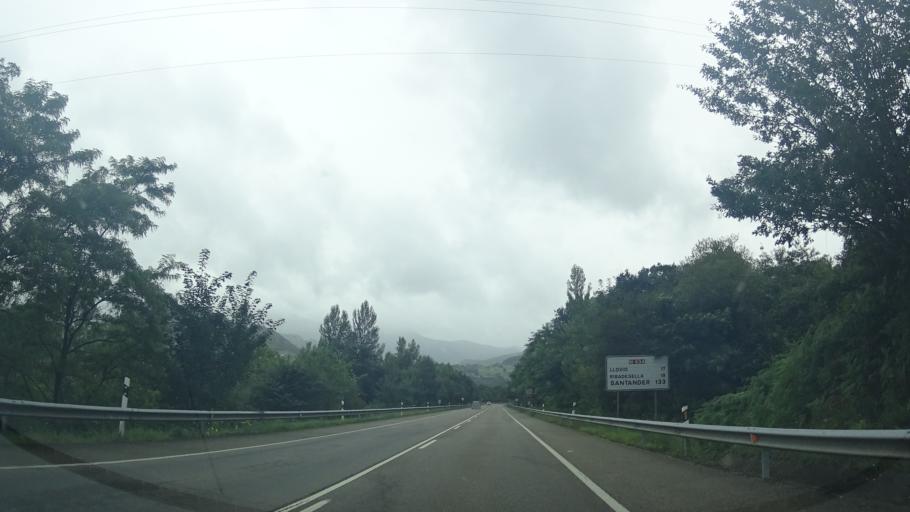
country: ES
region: Asturias
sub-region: Province of Asturias
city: Parres
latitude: 43.3783
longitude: -5.1802
